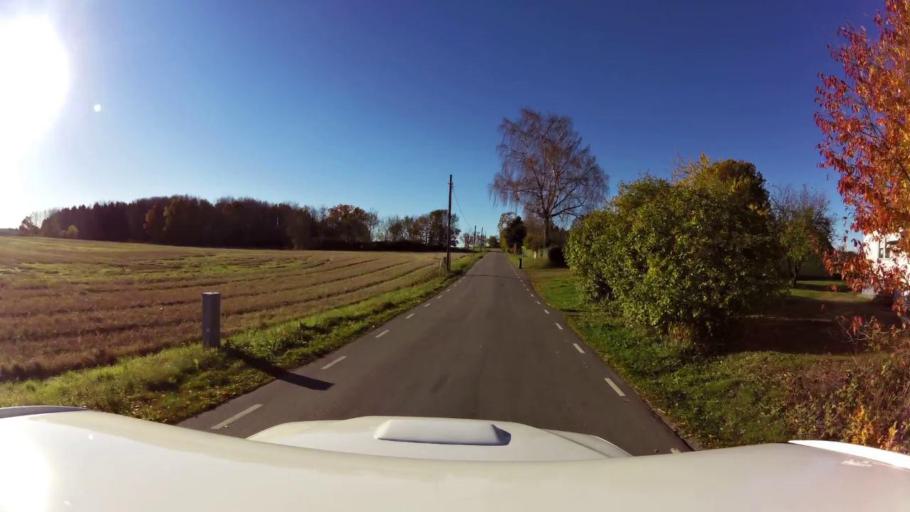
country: SE
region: OEstergoetland
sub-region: Linkopings Kommun
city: Ljungsbro
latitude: 58.5202
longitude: 15.4236
